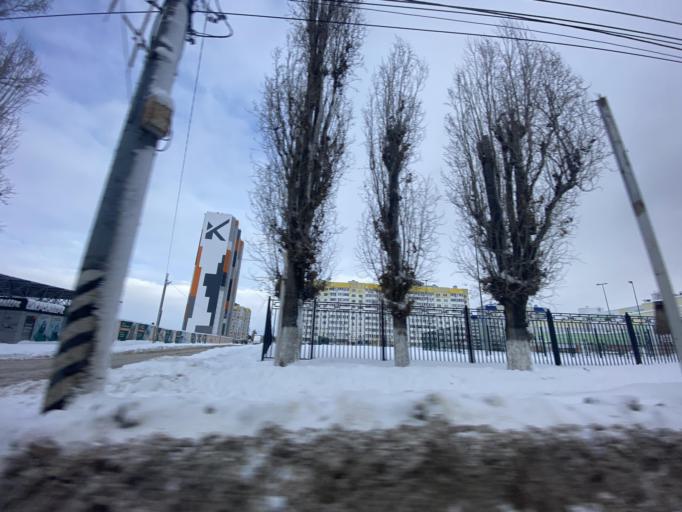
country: RU
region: Saratov
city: Engel's
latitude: 51.4985
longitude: 46.0881
